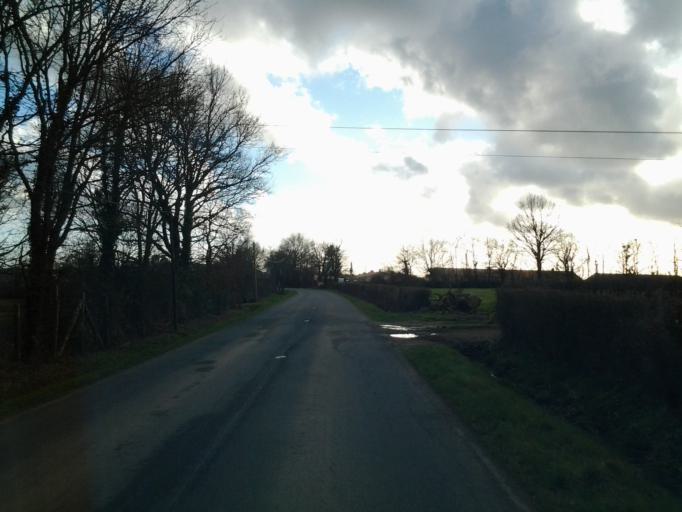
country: FR
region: Pays de la Loire
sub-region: Departement de la Vendee
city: Chateau-Guibert
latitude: 46.6170
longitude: -1.2365
